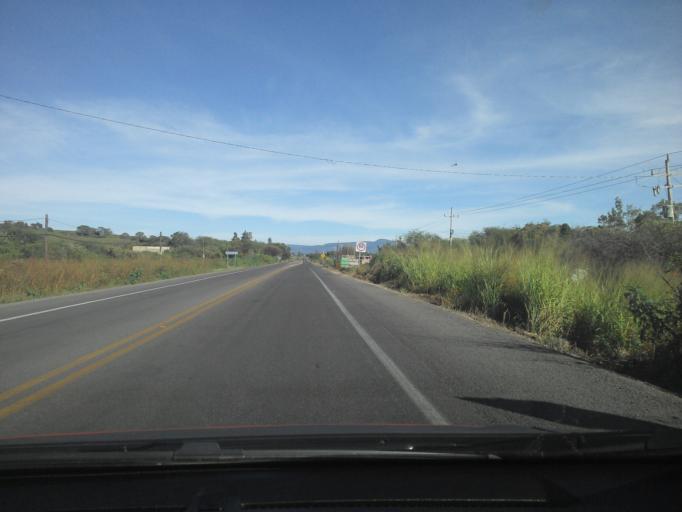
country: MX
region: Jalisco
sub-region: Teuchitlan
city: La Estanzuela
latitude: 20.6739
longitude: -103.8287
